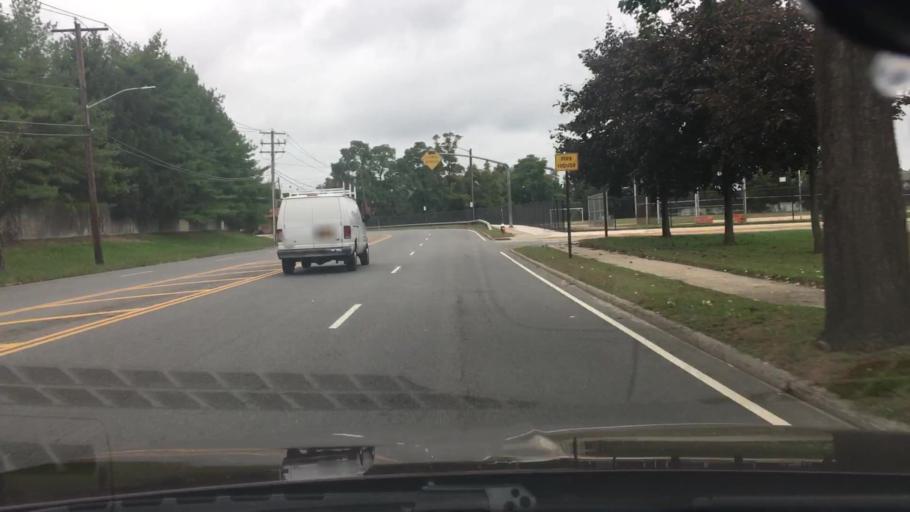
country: US
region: New York
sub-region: Nassau County
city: Jericho
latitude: 40.7781
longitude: -73.5533
